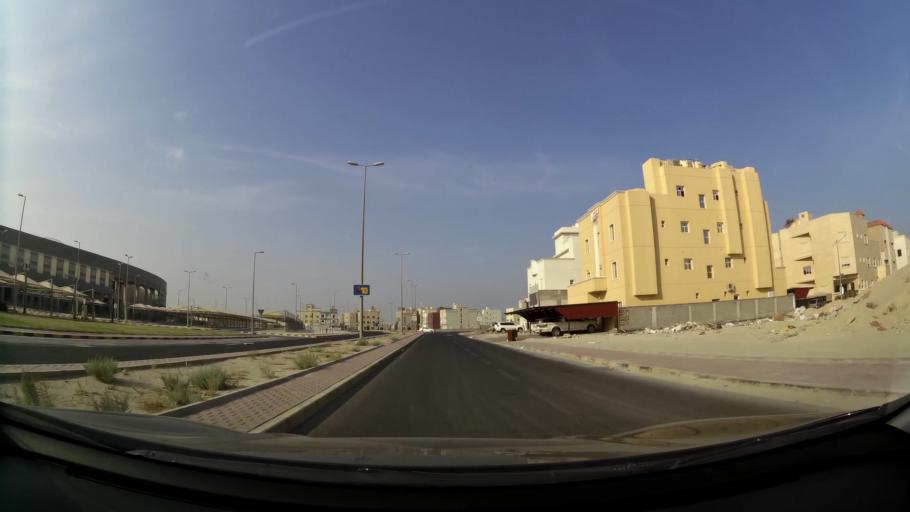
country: KW
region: Mubarak al Kabir
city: Mubarak al Kabir
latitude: 29.1962
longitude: 48.1030
